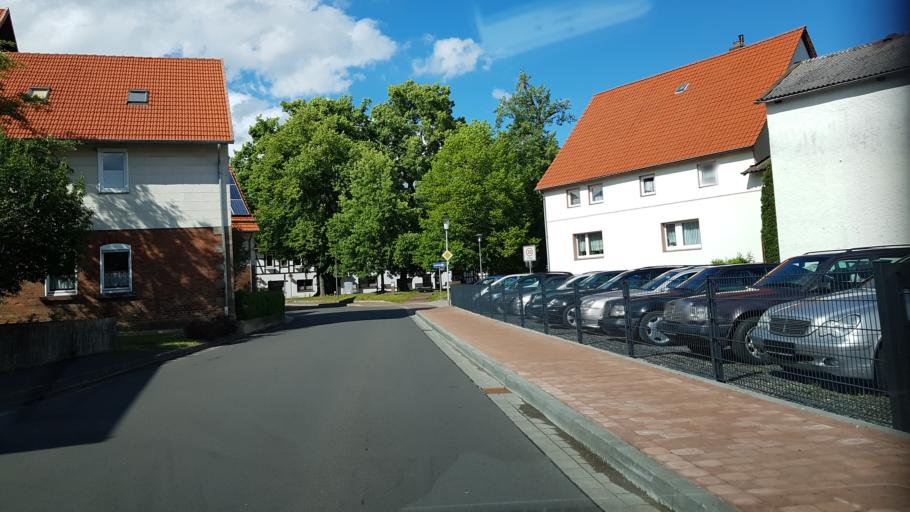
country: DE
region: Lower Saxony
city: Hardegsen
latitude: 51.6184
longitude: 9.8508
